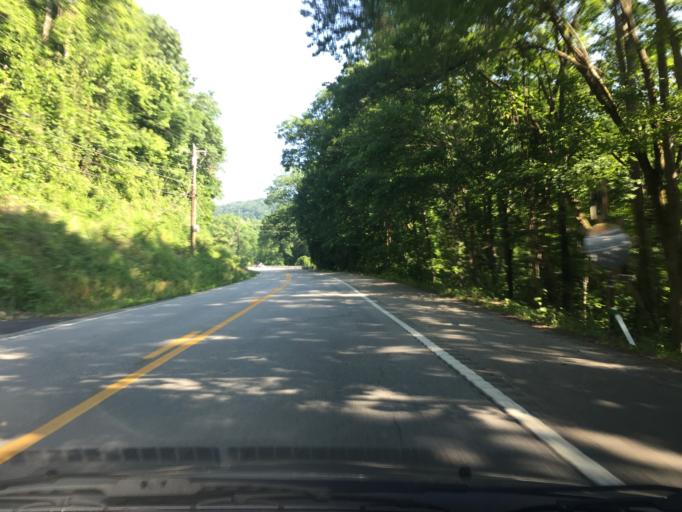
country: US
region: Tennessee
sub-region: Hamilton County
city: Lookout Mountain
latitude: 35.0320
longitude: -85.4073
